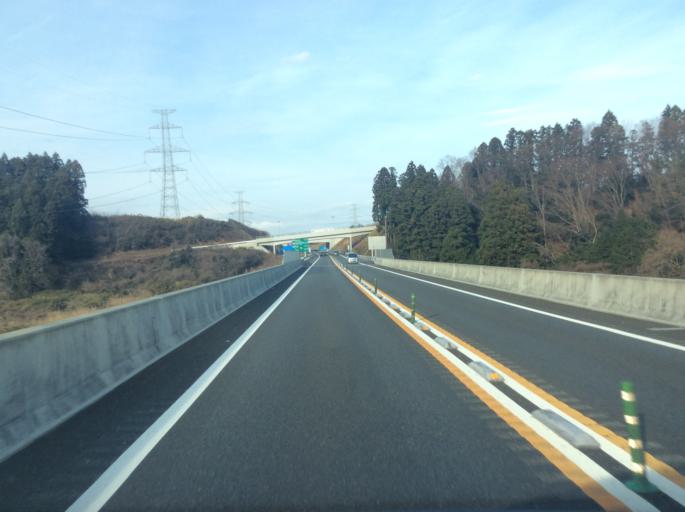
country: JP
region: Fukushima
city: Namie
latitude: 37.5090
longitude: 140.9429
